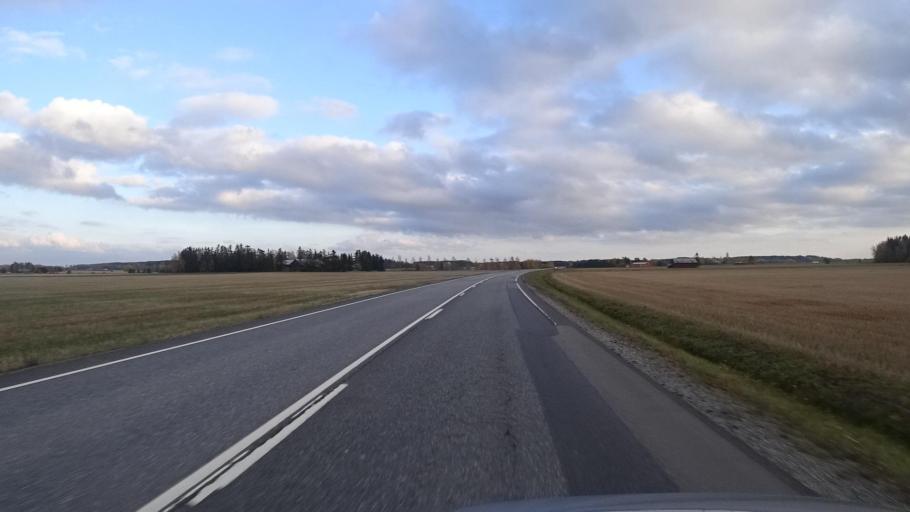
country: FI
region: Varsinais-Suomi
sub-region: Loimaa
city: Alastaro
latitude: 60.8979
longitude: 22.9541
